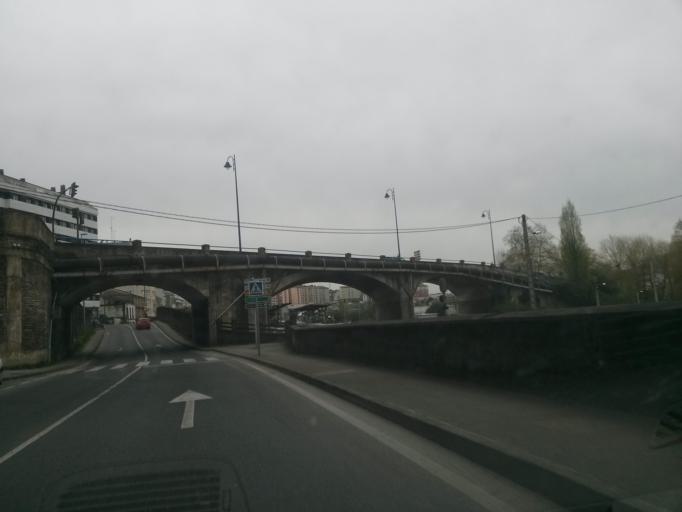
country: ES
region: Galicia
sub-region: Provincia de Lugo
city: Lugo
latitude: 43.0140
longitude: -7.5502
